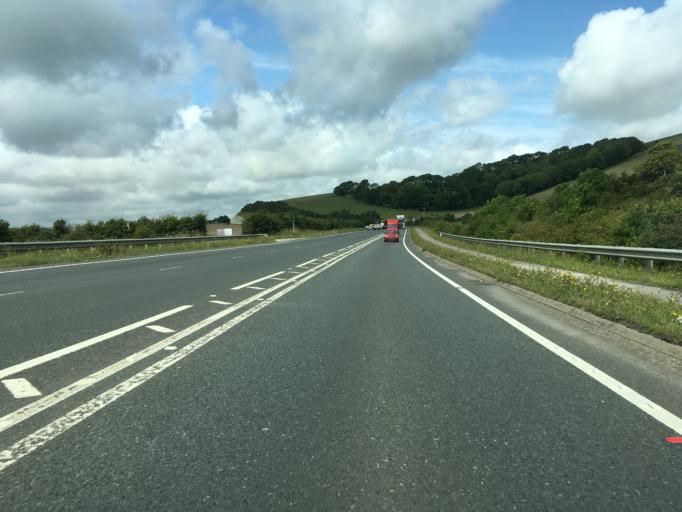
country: GB
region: England
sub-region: East Sussex
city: Ringmer
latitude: 50.8574
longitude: 0.0445
